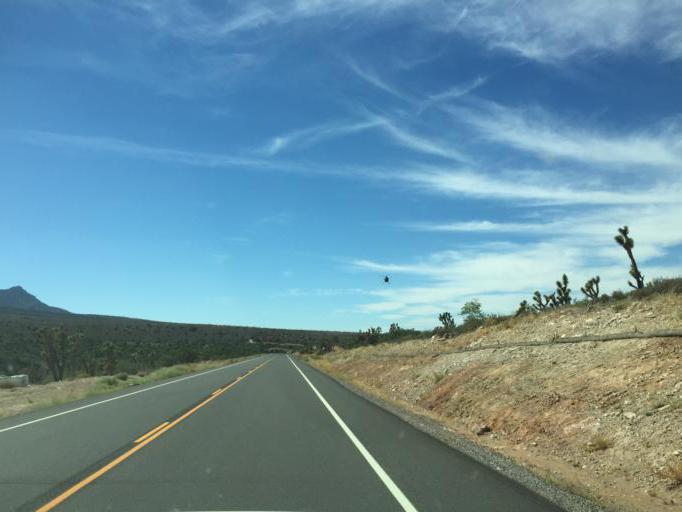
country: US
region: Arizona
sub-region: Mohave County
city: Meadview
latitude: 35.8783
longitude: -113.9806
